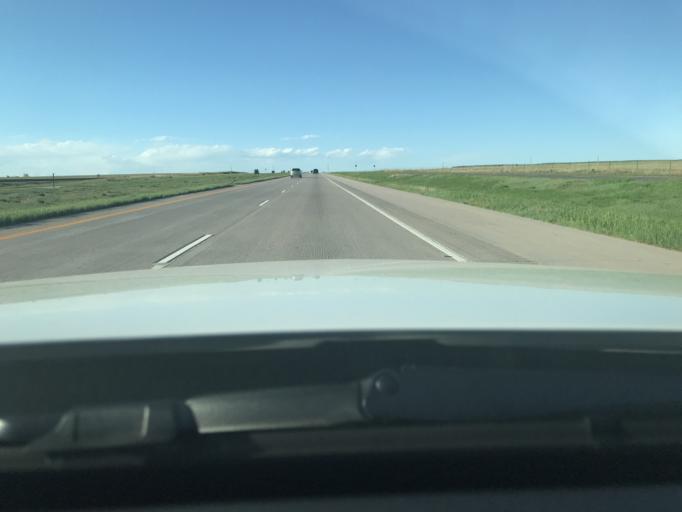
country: US
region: Colorado
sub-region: Larimer County
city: Wellington
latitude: 40.8089
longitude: -104.9766
